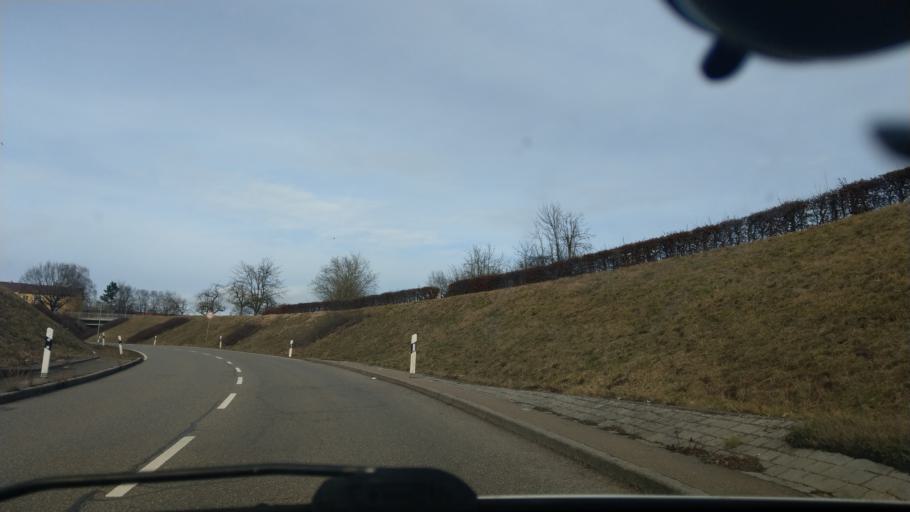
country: DE
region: Baden-Wuerttemberg
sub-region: Regierungsbezirk Stuttgart
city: Ostfildern
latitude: 48.7225
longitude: 9.2743
